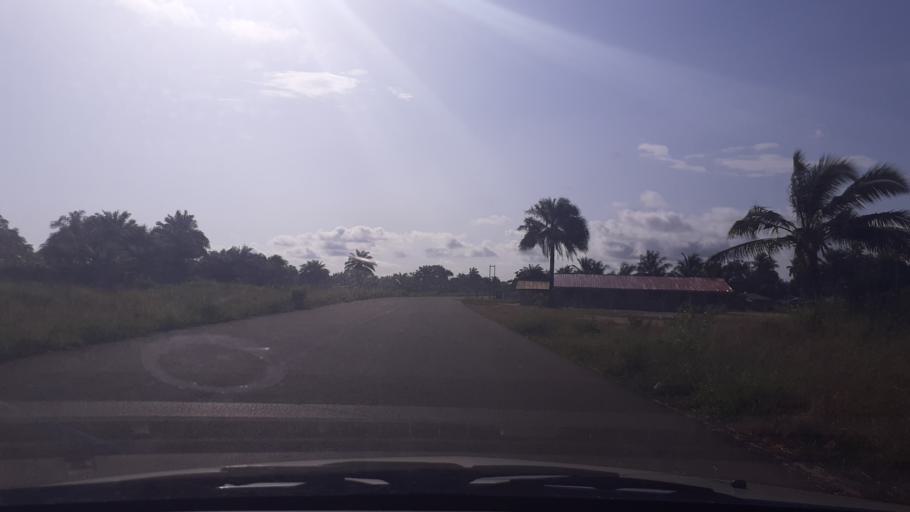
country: LR
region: Montserrado
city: Bensonville City
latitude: 6.1685
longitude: -10.4441
